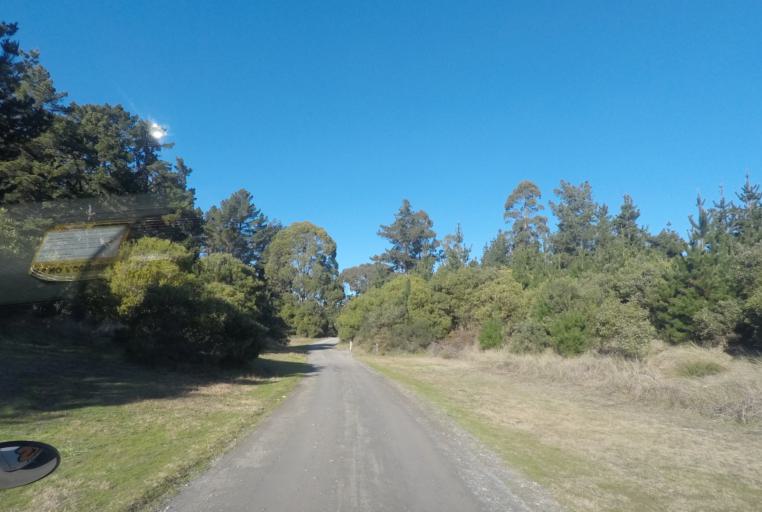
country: NZ
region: Tasman
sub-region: Tasman District
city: Mapua
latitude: -41.2635
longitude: 173.1425
